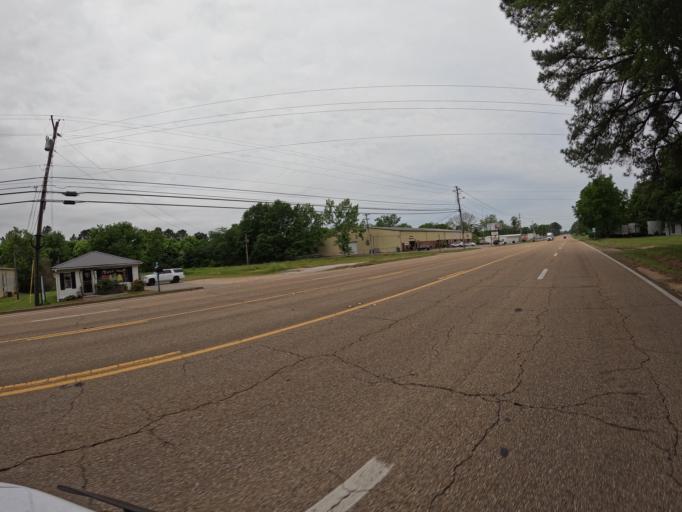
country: US
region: Mississippi
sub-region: Lee County
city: Tupelo
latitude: 34.2921
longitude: -88.7540
